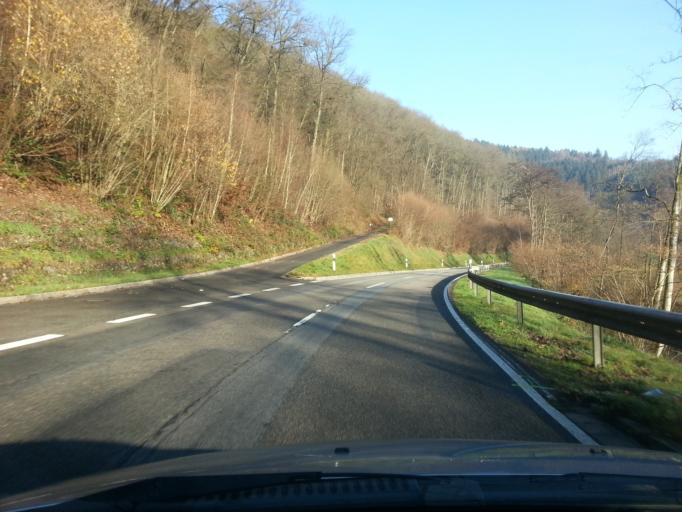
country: DE
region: Baden-Wuerttemberg
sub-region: Karlsruhe Region
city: Eberbach
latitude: 49.4899
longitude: 9.0407
